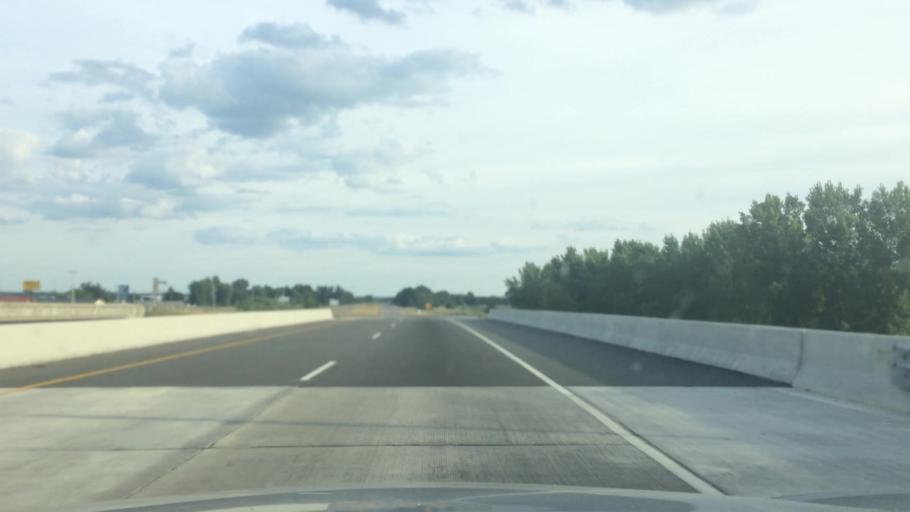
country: US
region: Wisconsin
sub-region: Portage County
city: Plover
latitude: 44.2143
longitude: -89.5248
